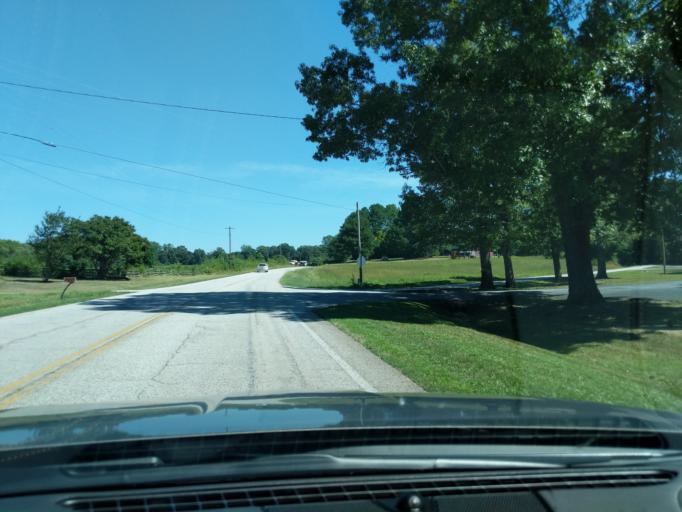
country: US
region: Georgia
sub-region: Habersham County
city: Demorest
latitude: 34.6098
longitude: -83.6144
